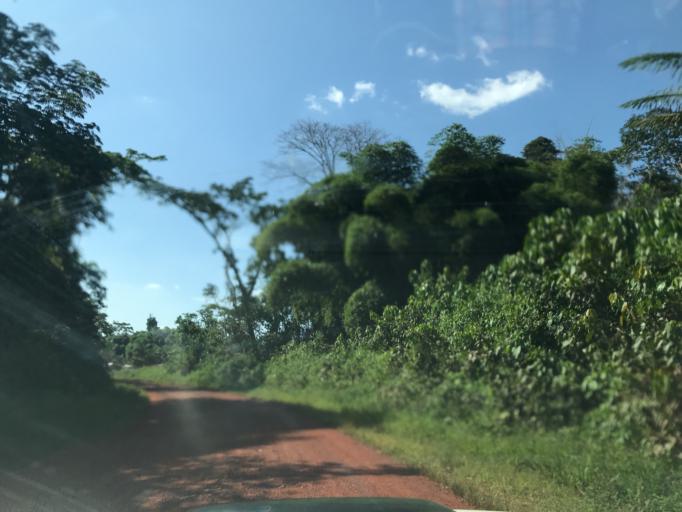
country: CD
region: Eastern Province
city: Kisangani
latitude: 1.2959
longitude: 25.2730
